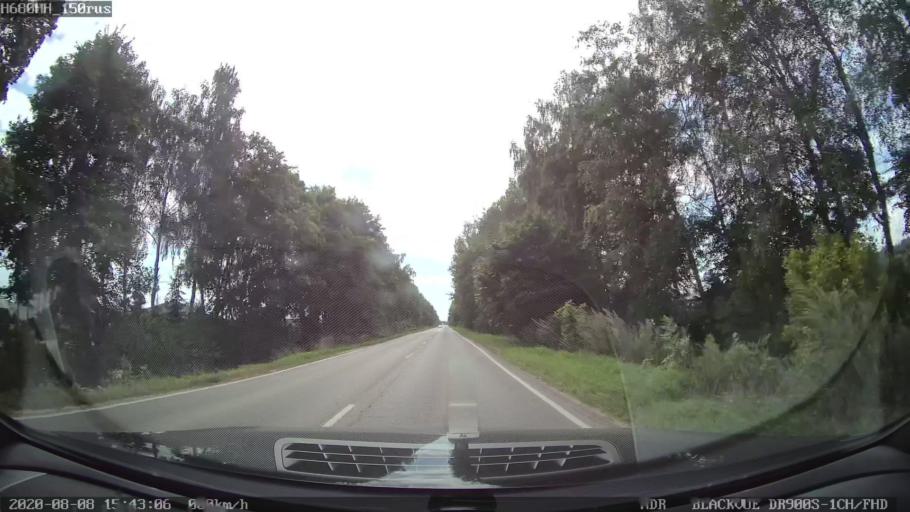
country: RU
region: Tula
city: Zaokskiy
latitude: 54.7347
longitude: 37.3484
